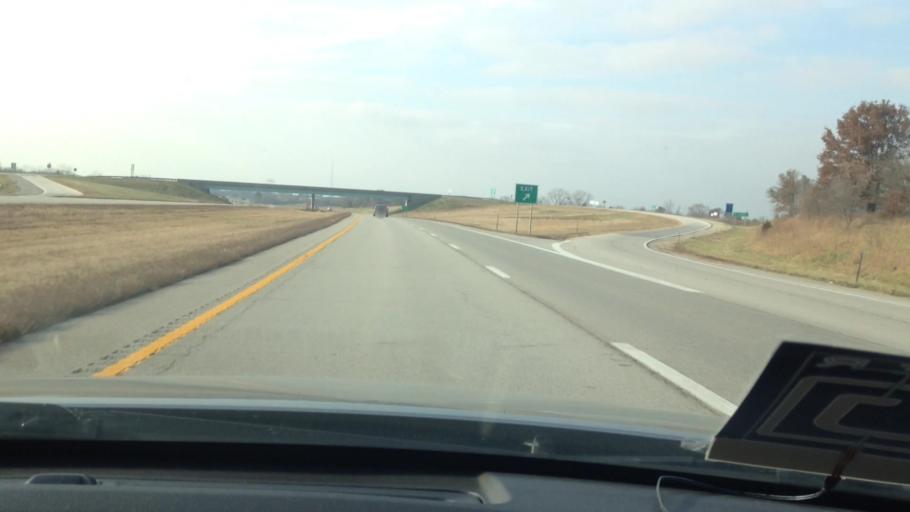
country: US
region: Missouri
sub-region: Cass County
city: Garden City
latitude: 38.5007
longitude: -94.0687
